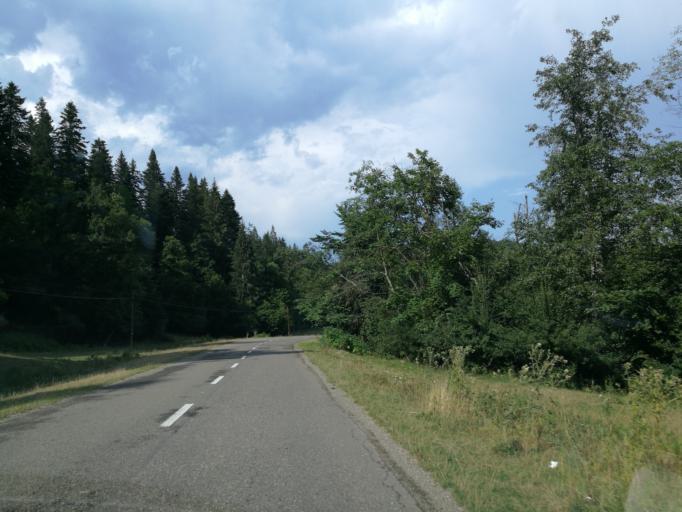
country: RO
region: Neamt
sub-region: Comuna Pipirig
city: Stanca
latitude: 47.1958
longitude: 26.1790
